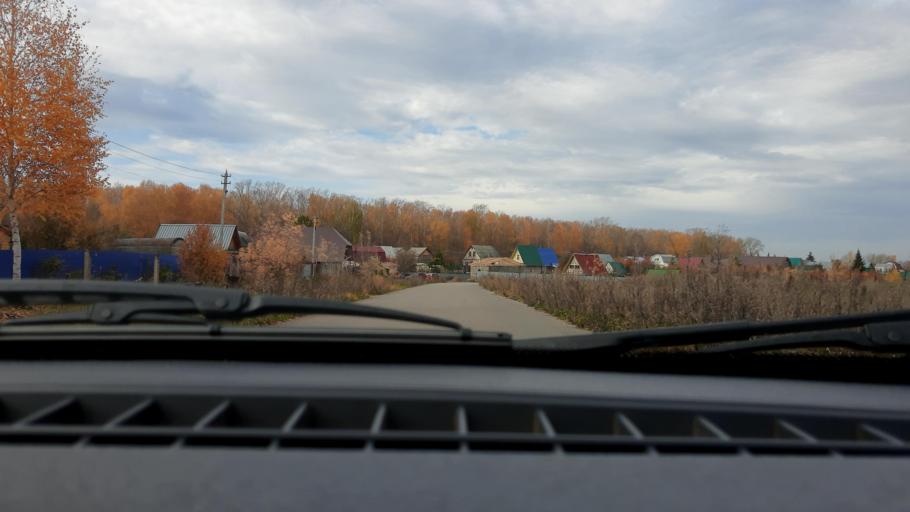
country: RU
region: Bashkortostan
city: Ufa
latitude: 54.5949
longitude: 55.9009
